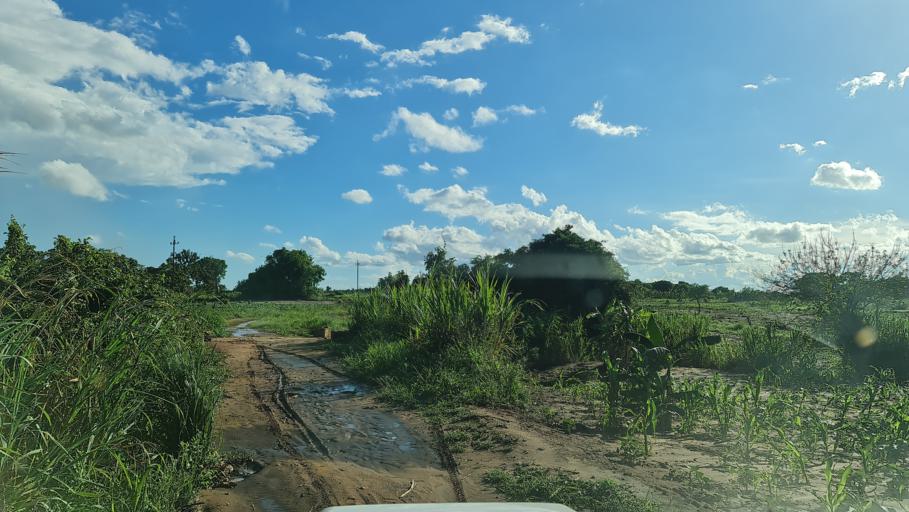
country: MZ
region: Nampula
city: Ilha de Mocambique
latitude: -14.9335
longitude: 40.2132
